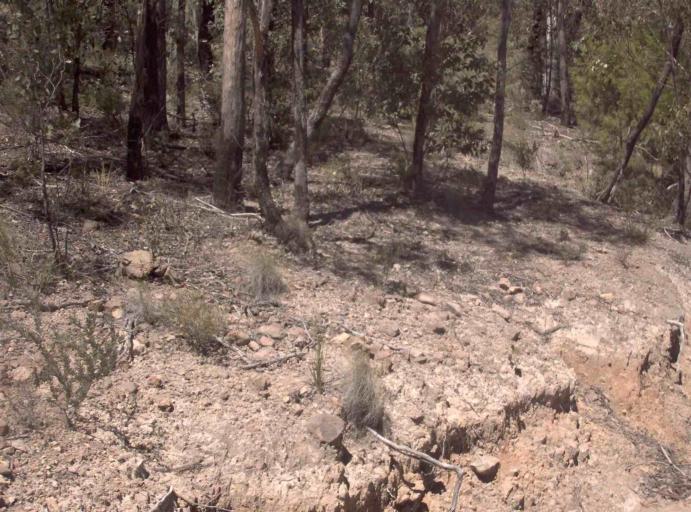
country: AU
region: New South Wales
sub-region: Snowy River
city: Jindabyne
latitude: -37.1226
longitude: 148.2483
